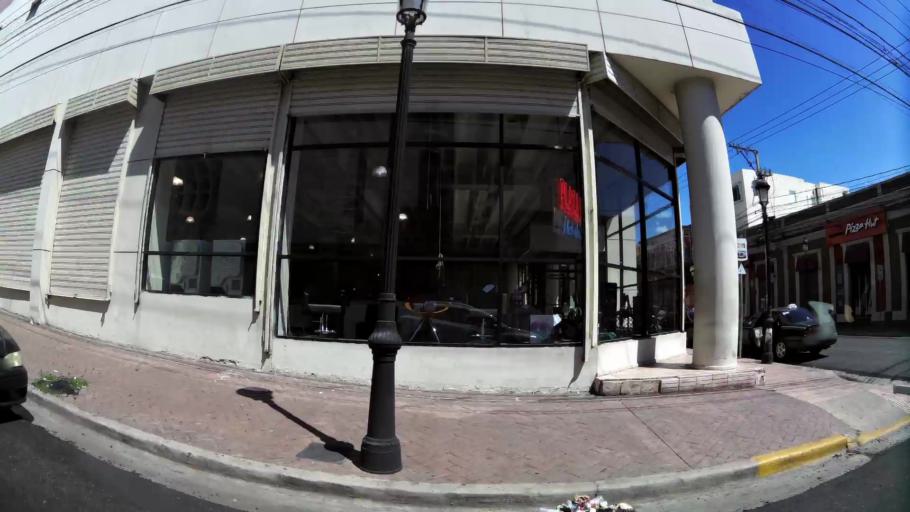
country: DO
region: Santiago
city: Santiago de los Caballeros
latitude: 19.4507
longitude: -70.7012
